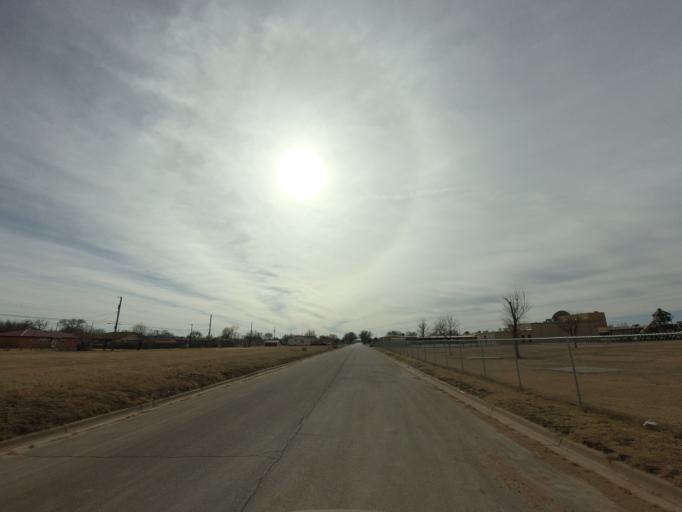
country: US
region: New Mexico
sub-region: Curry County
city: Clovis
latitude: 34.4117
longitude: -103.2405
